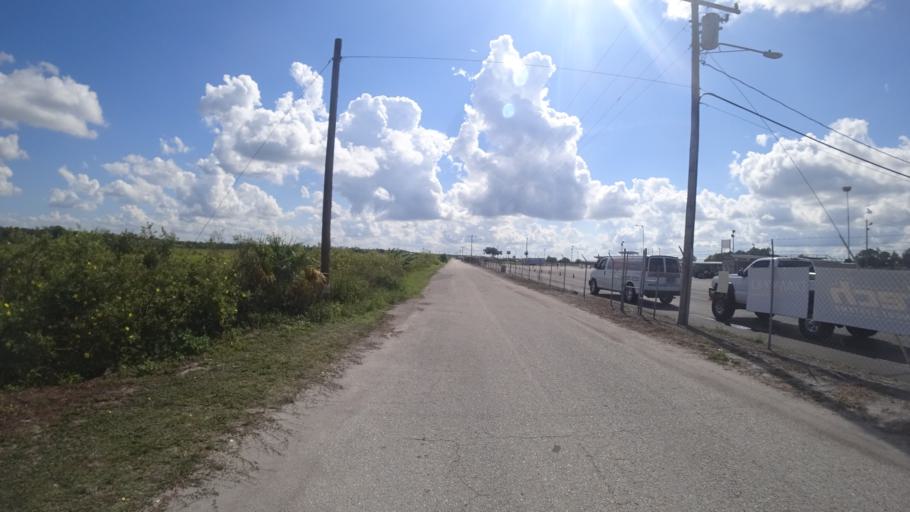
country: US
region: Florida
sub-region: Sarasota County
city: The Meadows
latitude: 27.4742
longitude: -82.3258
